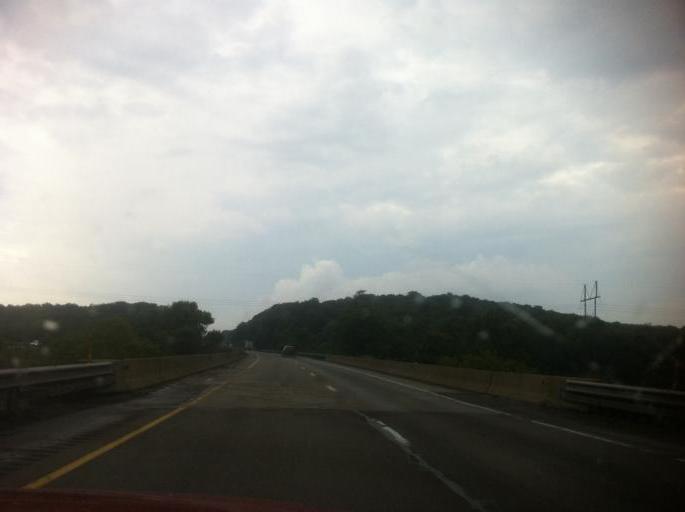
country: US
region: Pennsylvania
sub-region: Jefferson County
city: Brookville
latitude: 41.1605
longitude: -79.0019
